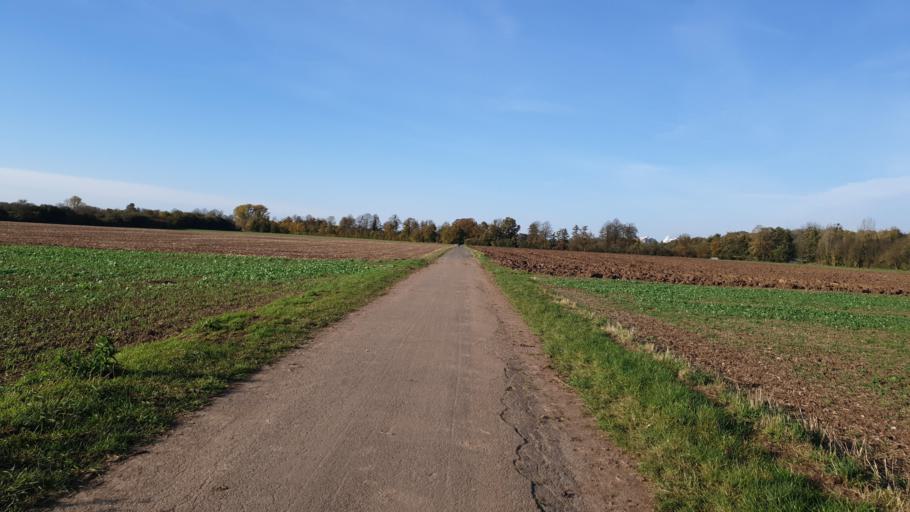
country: DE
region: North Rhine-Westphalia
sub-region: Regierungsbezirk Koln
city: Kerpen
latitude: 50.9202
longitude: 6.6924
